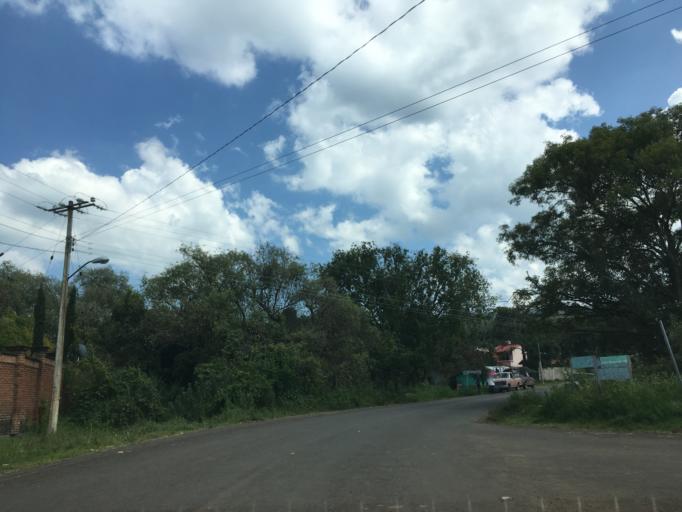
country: MX
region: Michoacan
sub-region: Morelia
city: Montana Monarca (Punta Altozano)
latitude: 19.5899
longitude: -101.1908
